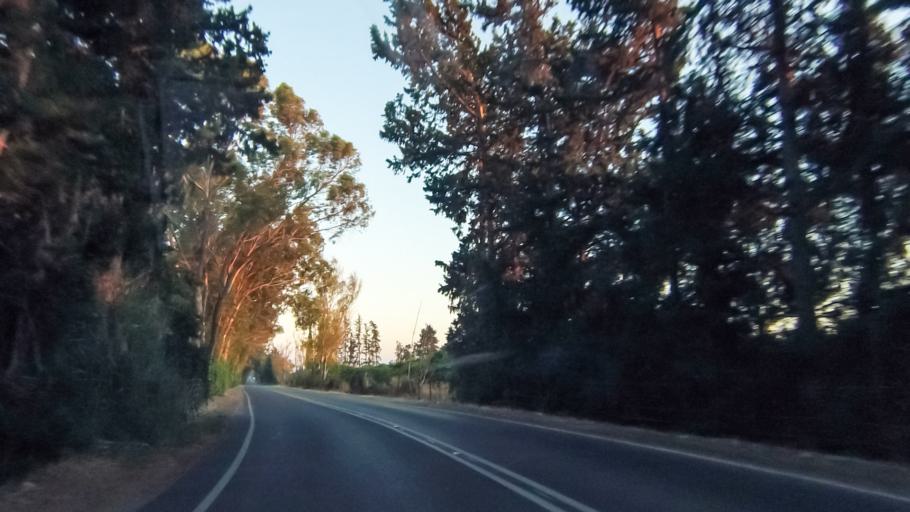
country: CY
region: Larnaka
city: Kolossi
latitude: 34.6516
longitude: 32.9421
